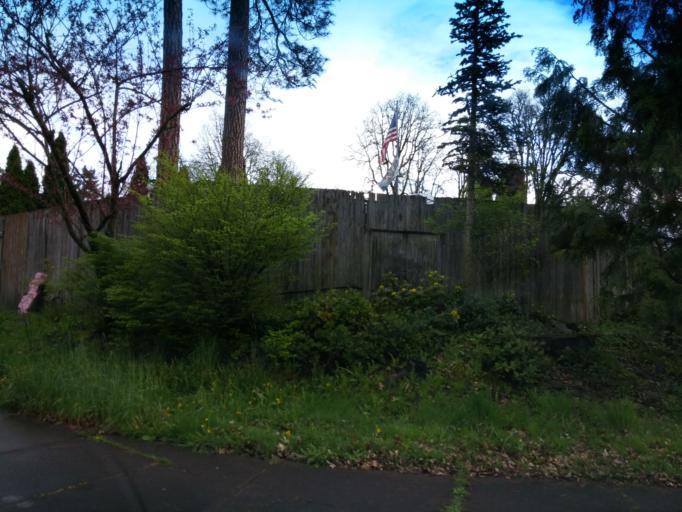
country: US
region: Oregon
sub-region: Washington County
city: Aloha
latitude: 45.5095
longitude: -122.8672
